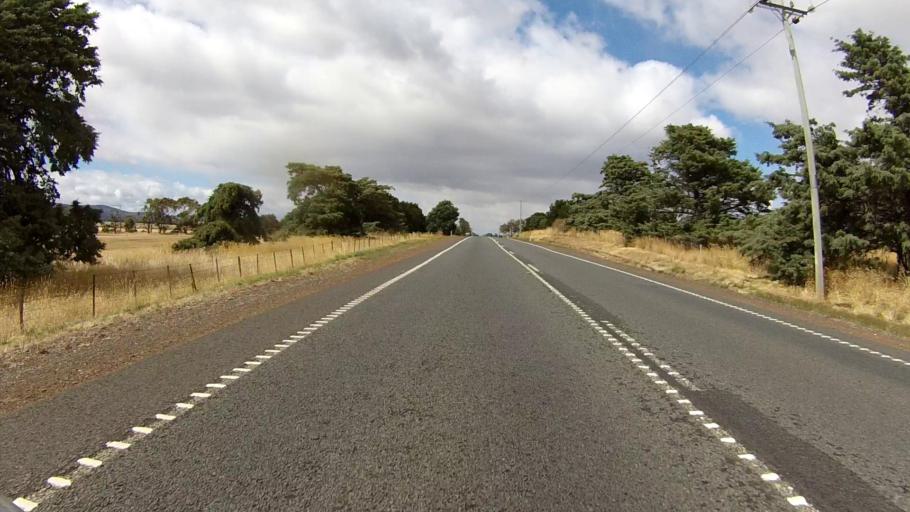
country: AU
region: Tasmania
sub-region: Northern Midlands
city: Evandale
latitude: -41.9521
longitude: 147.4953
